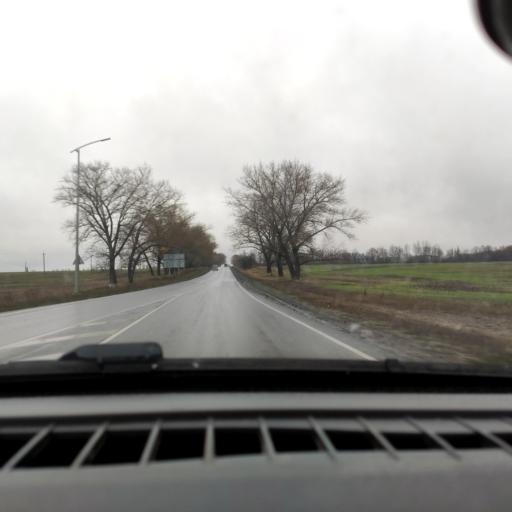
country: RU
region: Belgorod
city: Ilovka
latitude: 50.6892
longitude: 38.6606
